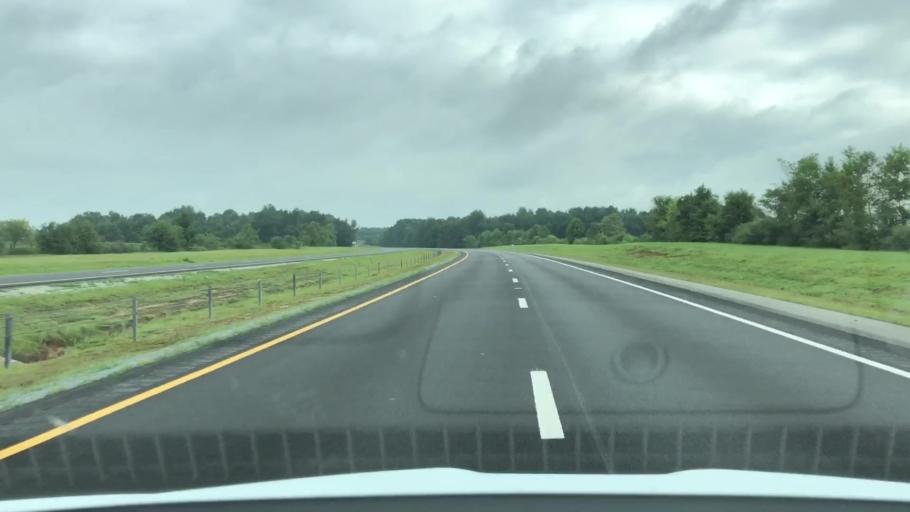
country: US
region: North Carolina
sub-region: Wayne County
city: Fremont
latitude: 35.5198
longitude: -77.9907
